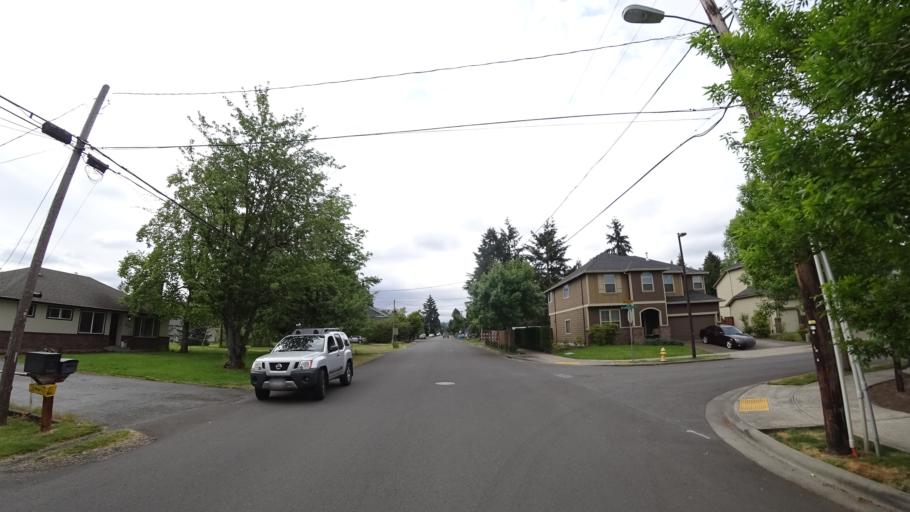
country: US
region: Oregon
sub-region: Washington County
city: Aloha
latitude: 45.5050
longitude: -122.8752
